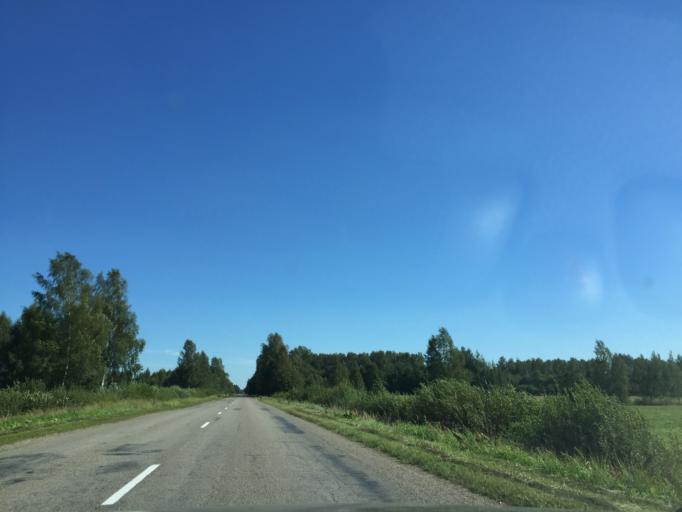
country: LV
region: Akniste
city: Akniste
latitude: 56.1528
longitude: 25.7716
